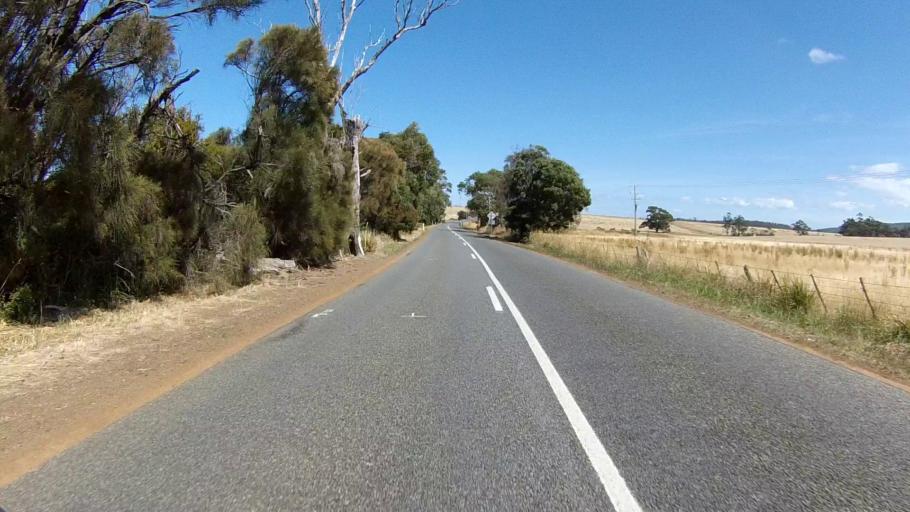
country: AU
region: Tasmania
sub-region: Sorell
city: Sorell
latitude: -42.2434
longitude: 148.0115
